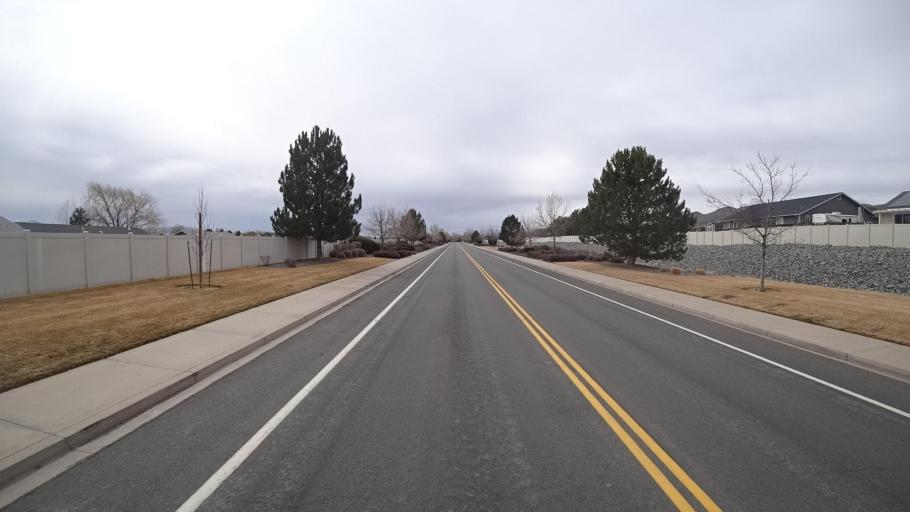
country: US
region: Nevada
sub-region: Washoe County
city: Spanish Springs
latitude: 39.6683
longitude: -119.7217
